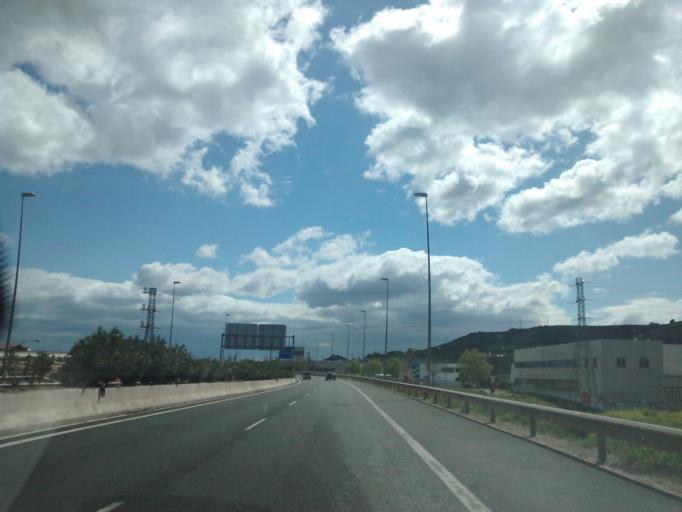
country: ES
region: La Rioja
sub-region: Provincia de La Rioja
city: Villamediana de Iregua
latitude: 42.4557
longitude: -2.4146
